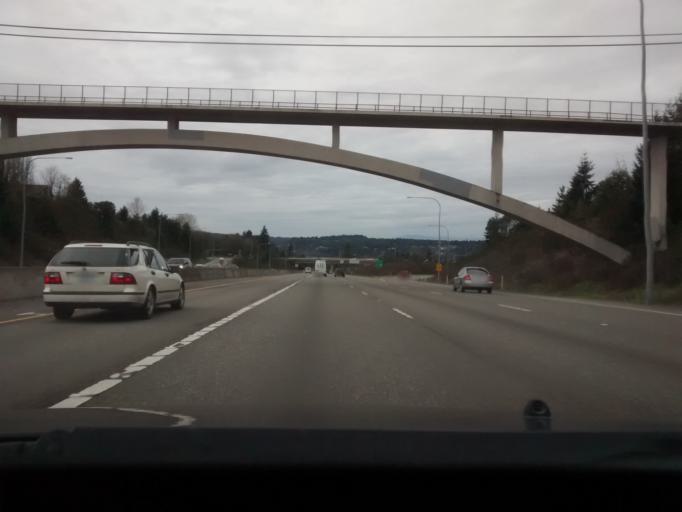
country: US
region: Washington
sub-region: Pierce County
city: Fircrest
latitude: 47.2588
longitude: -122.5308
